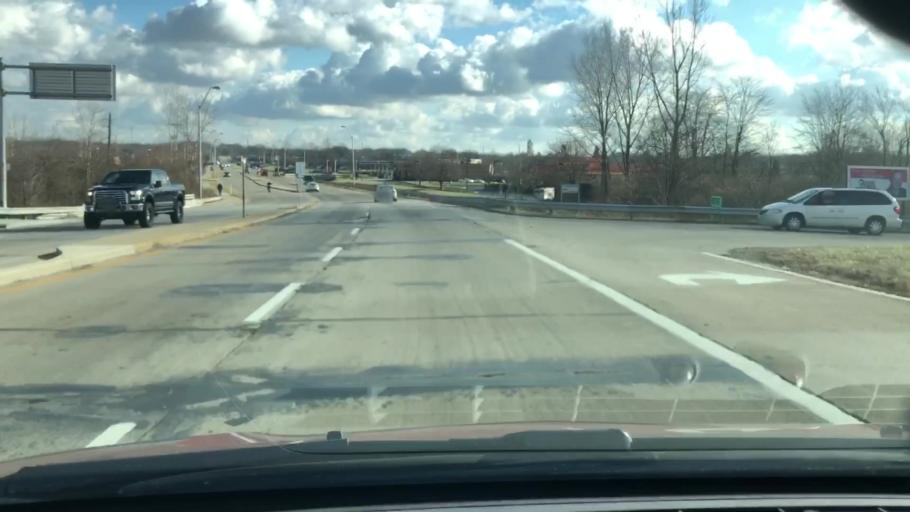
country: US
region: Ohio
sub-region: Greene County
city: Fairborn
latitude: 39.7829
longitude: -84.0014
